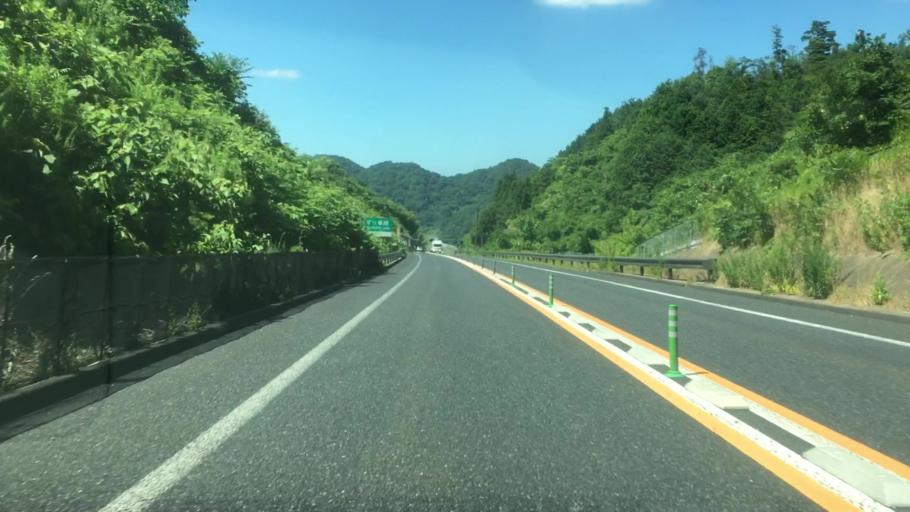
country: JP
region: Tottori
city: Tottori
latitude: 35.3673
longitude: 134.2025
